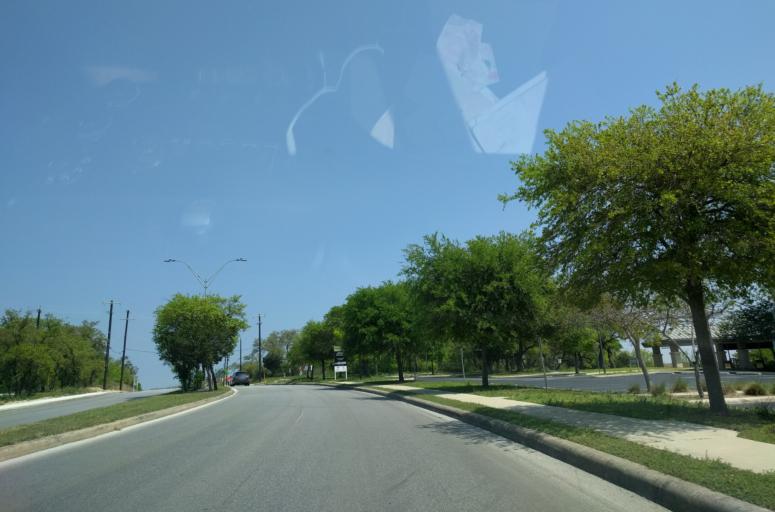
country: US
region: Texas
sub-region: Bexar County
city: Shavano Park
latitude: 29.5760
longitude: -98.5926
